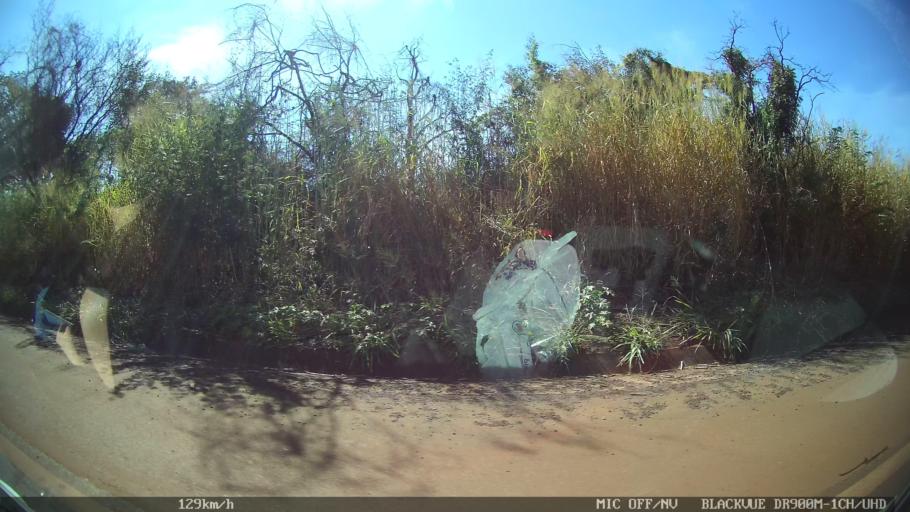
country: BR
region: Sao Paulo
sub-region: Ipua
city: Ipua
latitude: -20.4542
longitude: -48.1646
